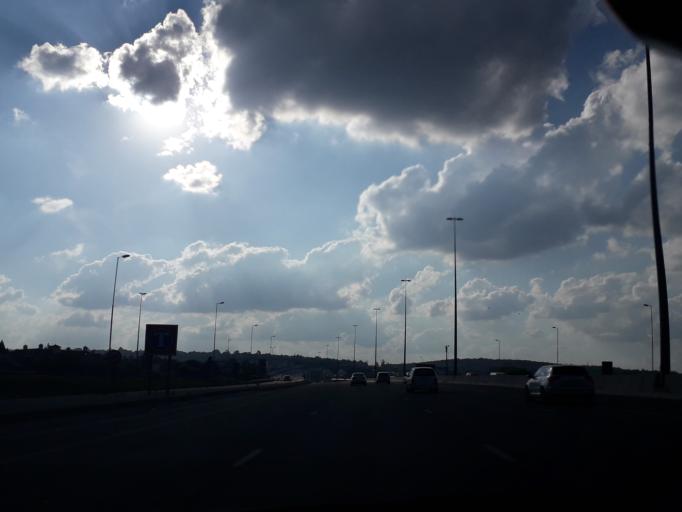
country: ZA
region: Gauteng
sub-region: City of Johannesburg Metropolitan Municipality
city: Midrand
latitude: -26.0390
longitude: 28.0634
